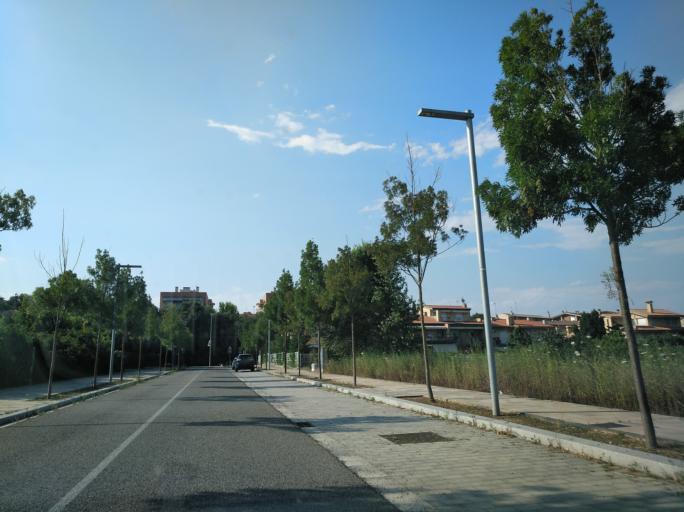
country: ES
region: Catalonia
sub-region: Provincia de Girona
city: Salt
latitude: 41.9910
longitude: 2.8041
